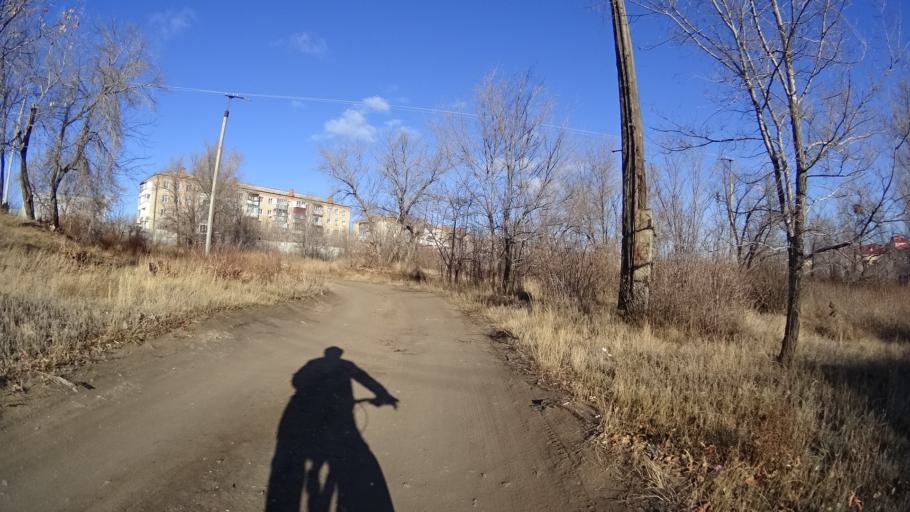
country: RU
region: Chelyabinsk
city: Troitsk
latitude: 54.0768
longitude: 61.5340
